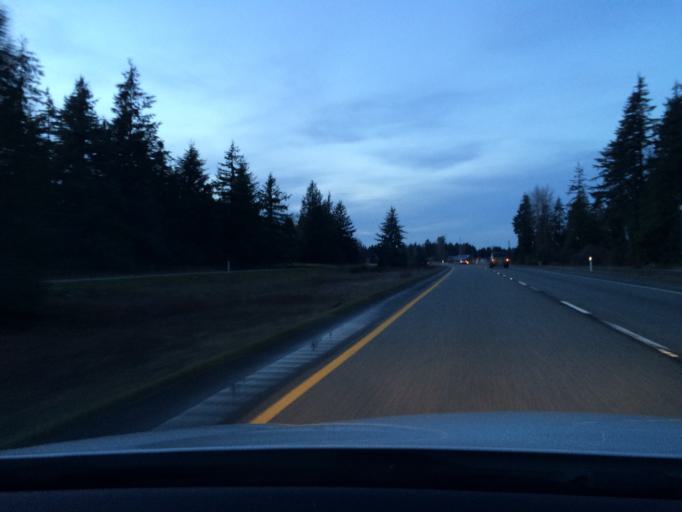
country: US
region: Washington
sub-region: Whatcom County
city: Ferndale
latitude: 48.9181
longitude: -122.6323
